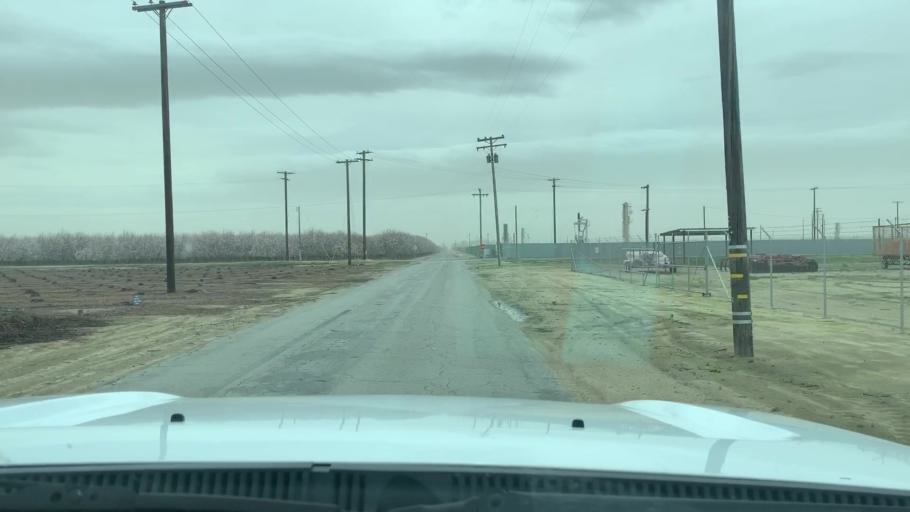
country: US
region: California
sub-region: Kern County
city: Shafter
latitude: 35.5303
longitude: -119.2689
